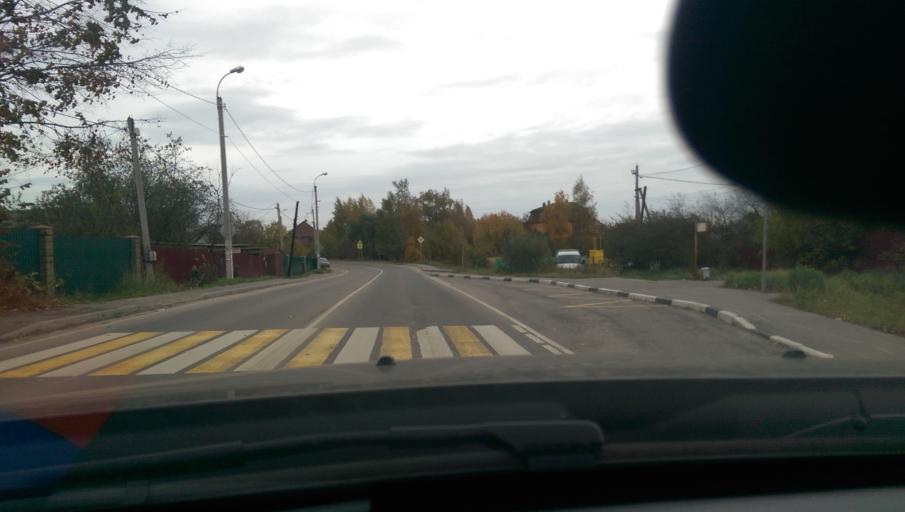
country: RU
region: Moskovskaya
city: Pirogovskiy
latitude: 56.0019
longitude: 37.7250
